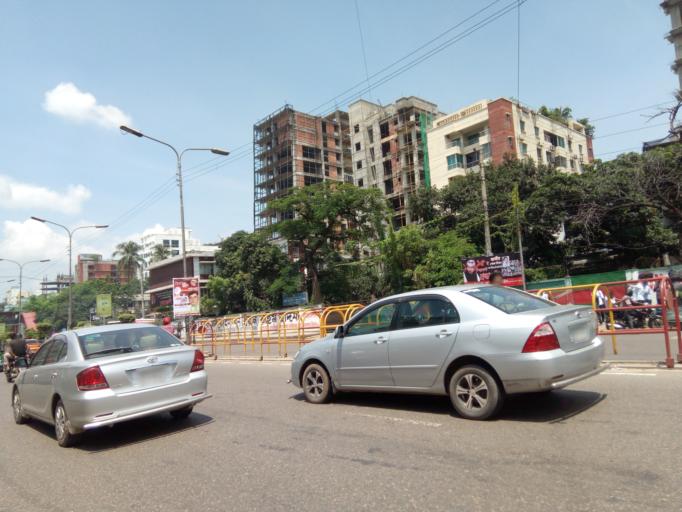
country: BD
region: Dhaka
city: Paltan
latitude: 23.7905
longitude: 90.4002
